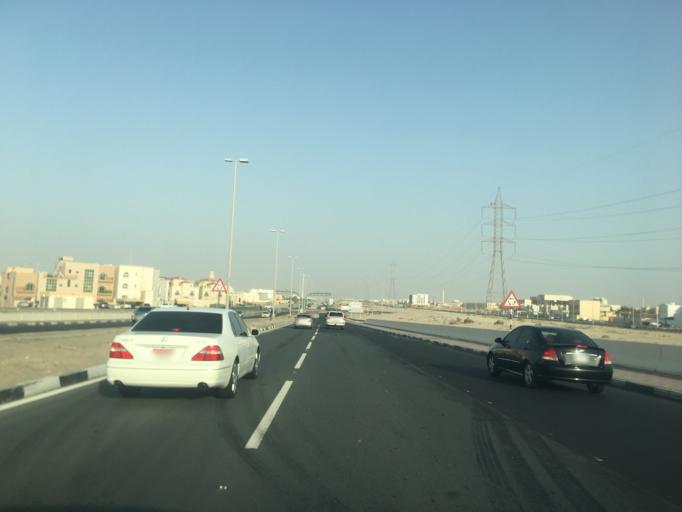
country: AE
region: Abu Dhabi
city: Abu Dhabi
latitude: 24.3244
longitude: 54.6251
